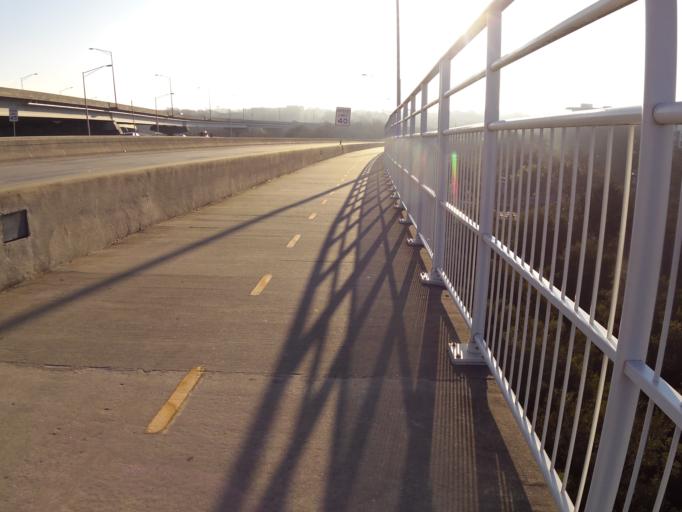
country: US
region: South Carolina
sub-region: Charleston County
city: Charleston
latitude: 32.8010
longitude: -79.9027
